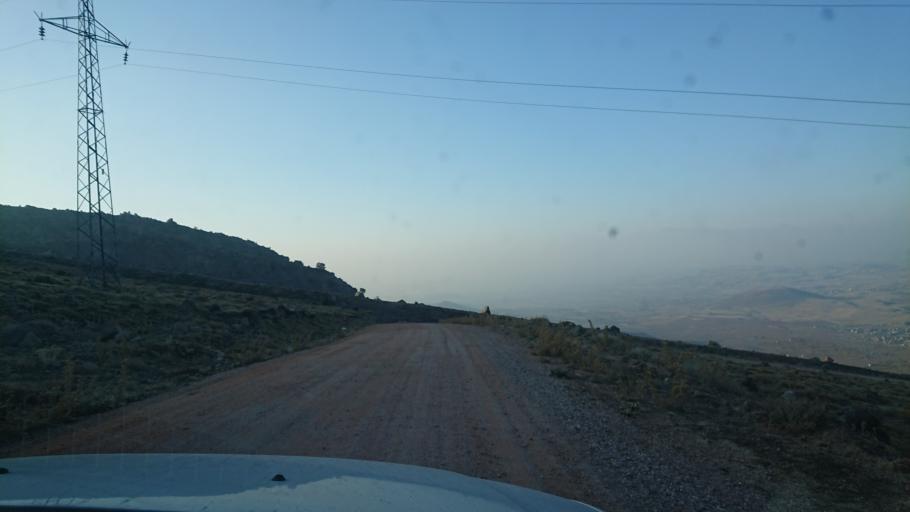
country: TR
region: Aksaray
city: Taspinar
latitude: 38.1623
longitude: 34.1774
